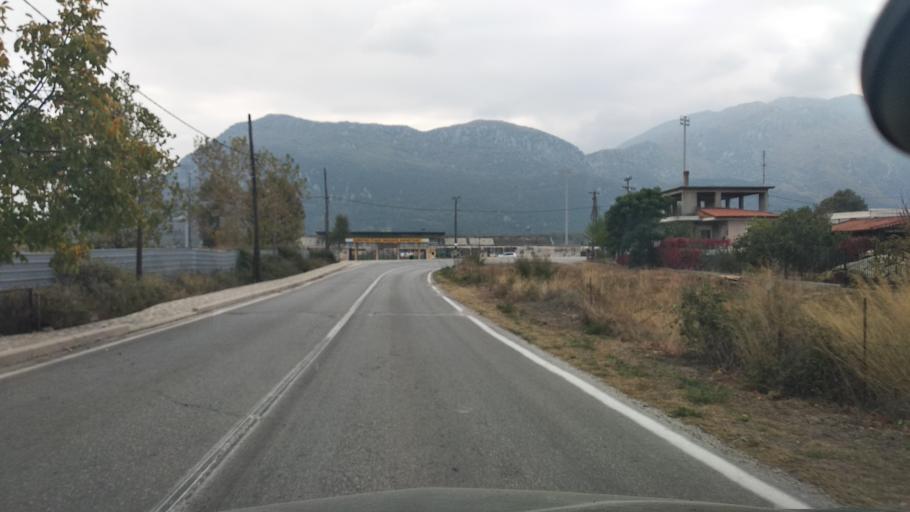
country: GR
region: Thessaly
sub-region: Trikala
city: Kalampaka
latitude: 39.7023
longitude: 21.6134
